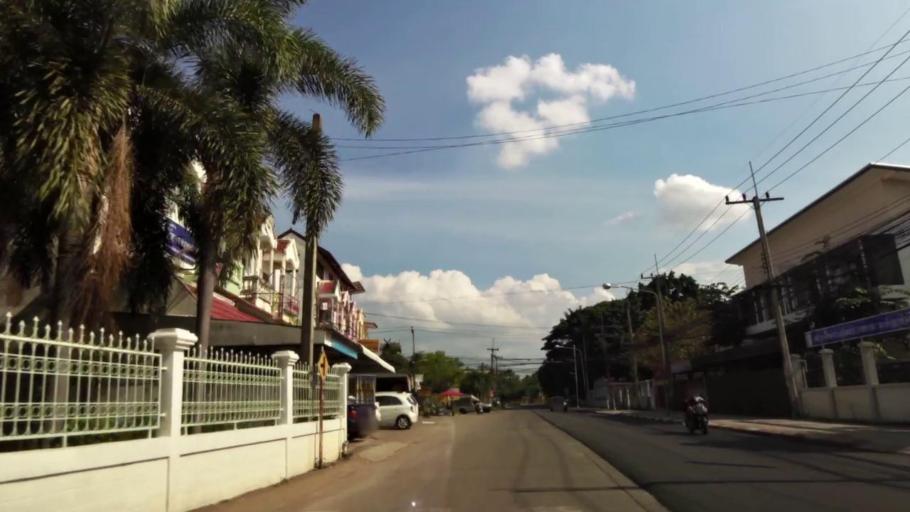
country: TH
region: Phrae
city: Phrae
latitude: 18.1350
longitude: 100.1365
